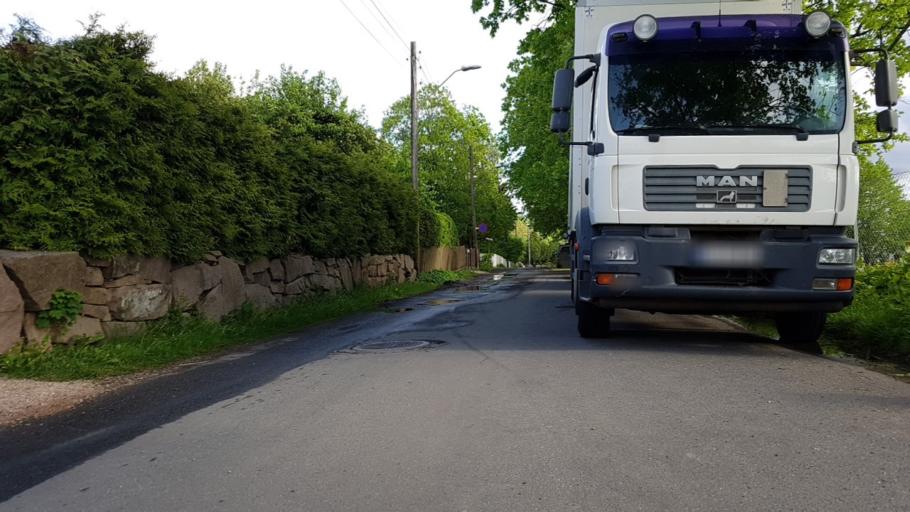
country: NO
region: Oslo
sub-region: Oslo
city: Oslo
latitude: 59.9422
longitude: 10.7888
